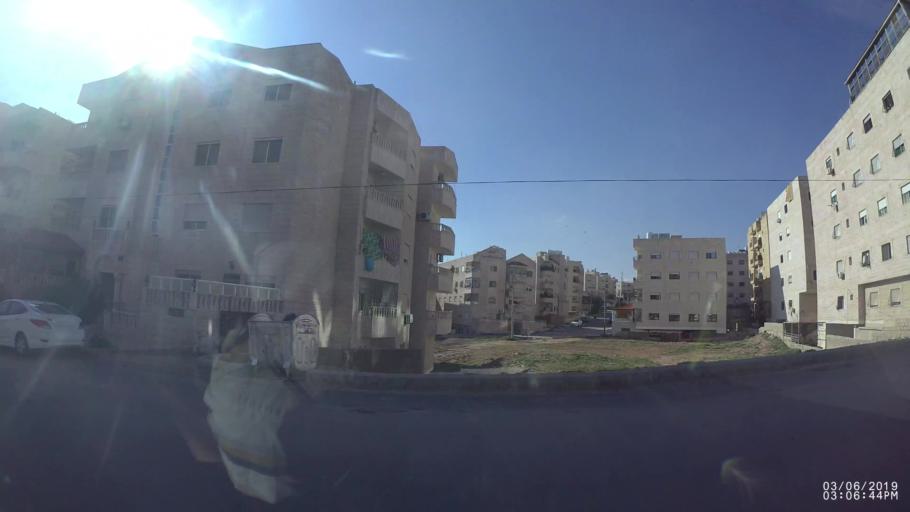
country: JO
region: Amman
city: Amman
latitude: 31.9785
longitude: 35.9393
